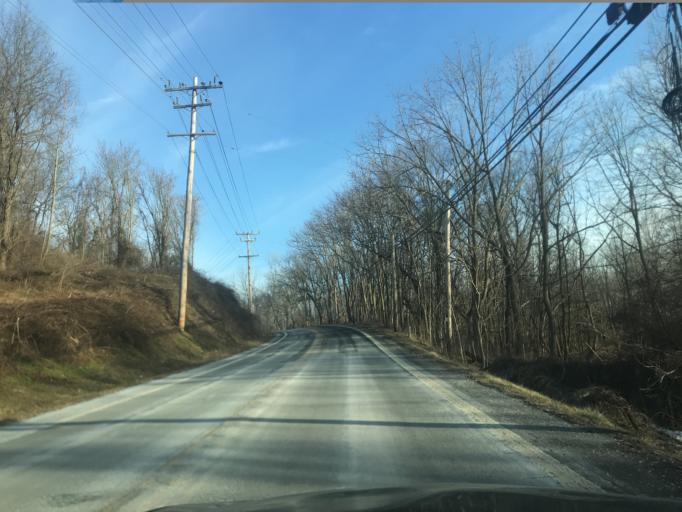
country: US
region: Maryland
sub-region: Carroll County
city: Sykesville
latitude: 39.3093
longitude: -76.9787
